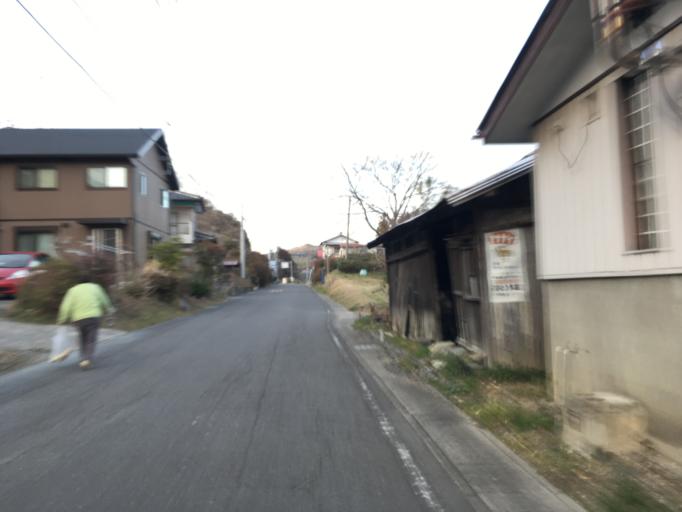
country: JP
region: Ibaraki
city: Daigo
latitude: 36.8080
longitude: 140.3703
